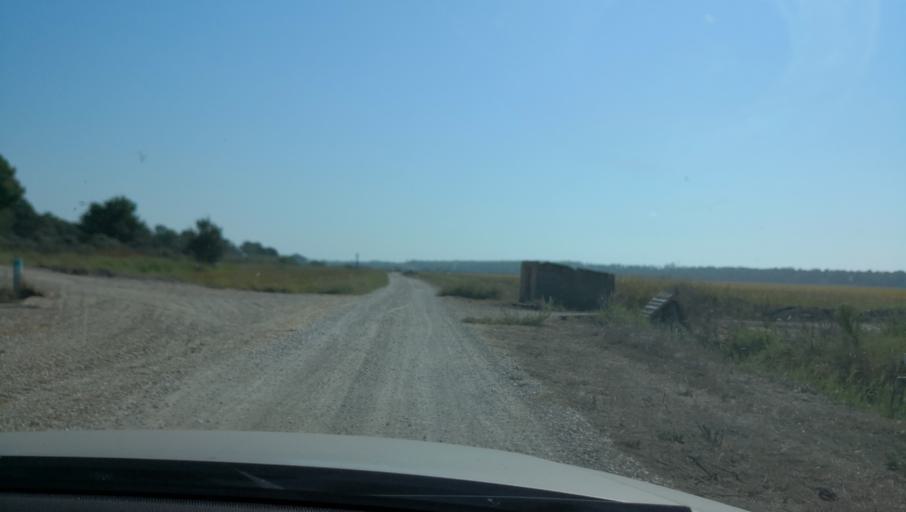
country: PT
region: Setubal
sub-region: Setubal
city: Setubal
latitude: 38.3933
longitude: -8.7888
